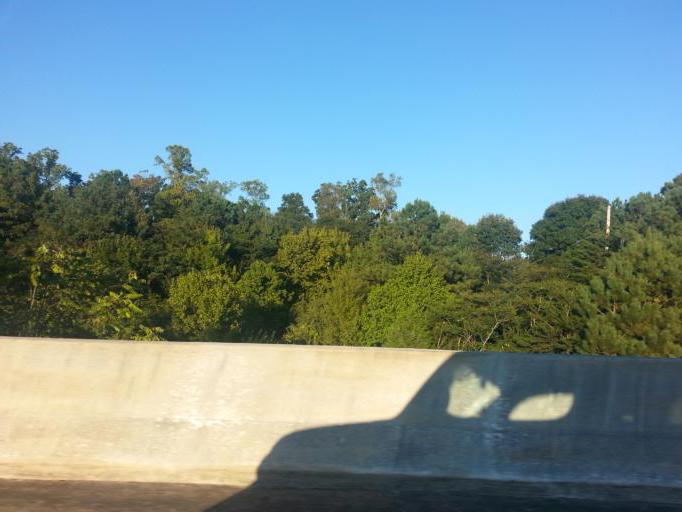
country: US
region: Tennessee
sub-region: Blount County
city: Alcoa
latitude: 35.8433
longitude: -83.9862
